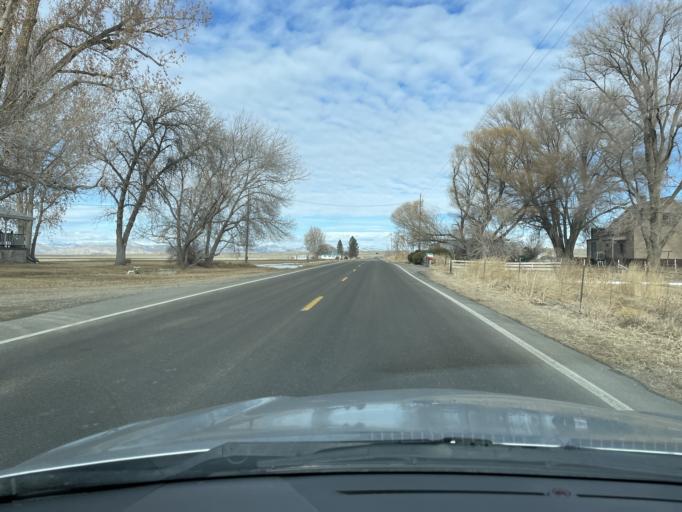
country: US
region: Colorado
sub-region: Mesa County
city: Loma
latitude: 39.2551
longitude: -108.8128
